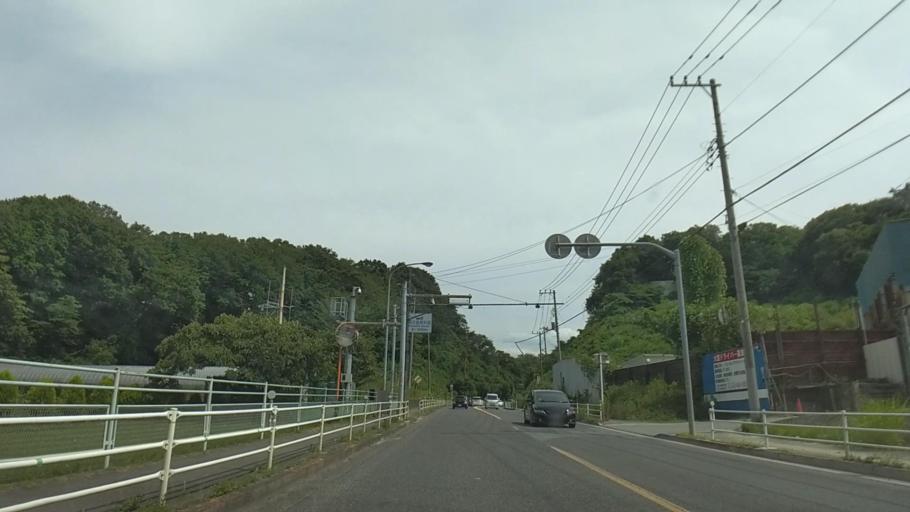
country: JP
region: Tokyo
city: Hachioji
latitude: 35.6232
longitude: 139.3401
